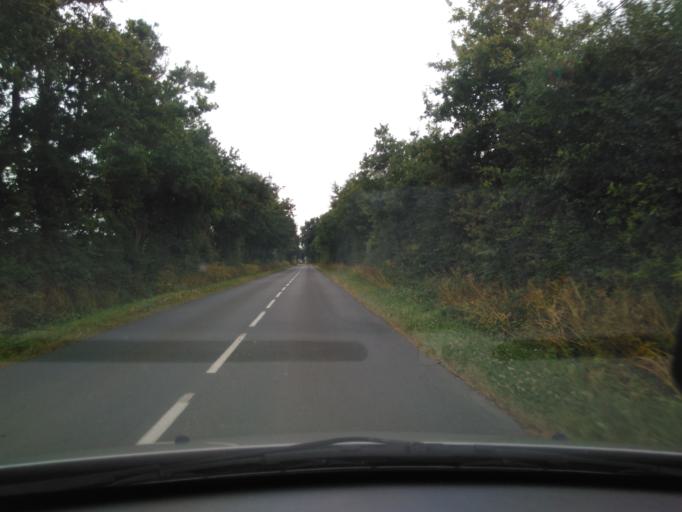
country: FR
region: Pays de la Loire
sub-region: Departement de la Vendee
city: Dompierre-sur-Yon
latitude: 46.7680
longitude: -1.3930
